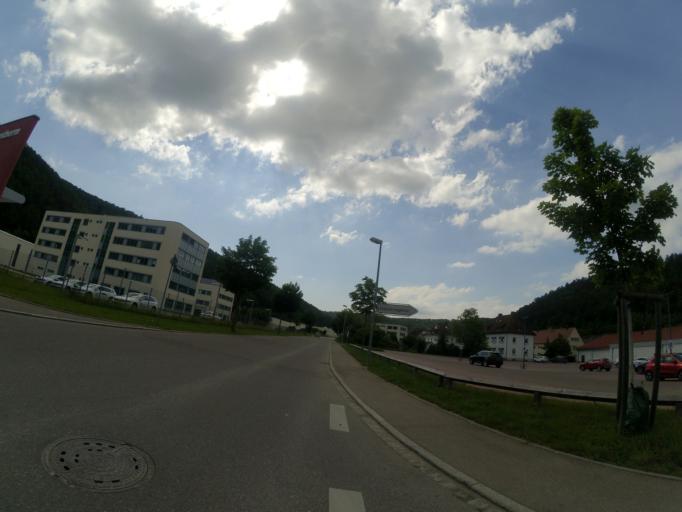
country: DE
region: Baden-Wuerttemberg
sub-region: Tuebingen Region
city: Blaubeuren
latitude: 48.4019
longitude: 9.7866
